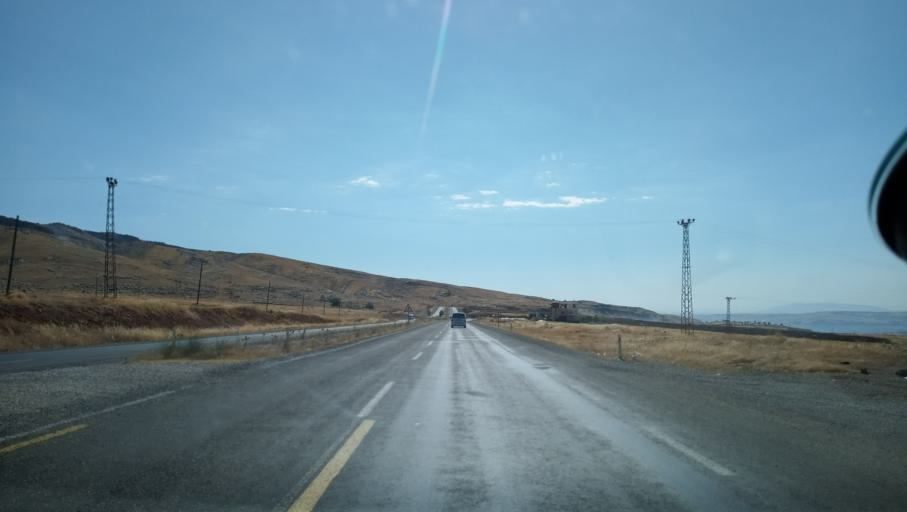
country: TR
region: Diyarbakir
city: Silvan
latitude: 38.1279
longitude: 41.0747
